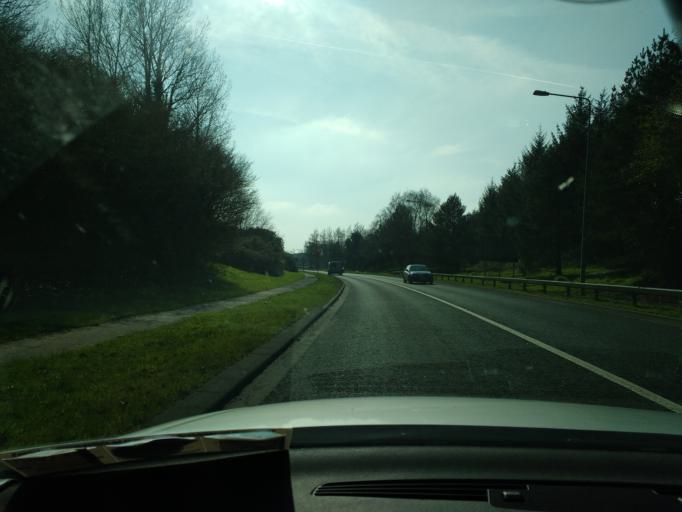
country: IE
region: Munster
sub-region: An Clar
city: Shannon
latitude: 52.7003
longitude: -8.8987
